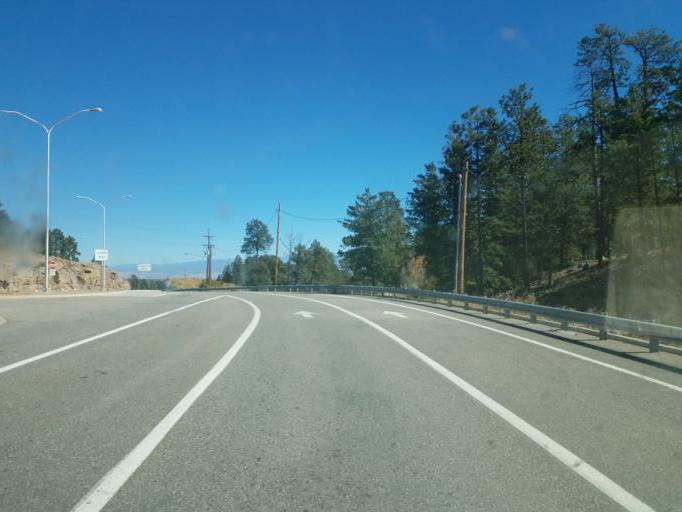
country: US
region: New Mexico
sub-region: Los Alamos County
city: Los Alamos
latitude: 35.8725
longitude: -106.3449
